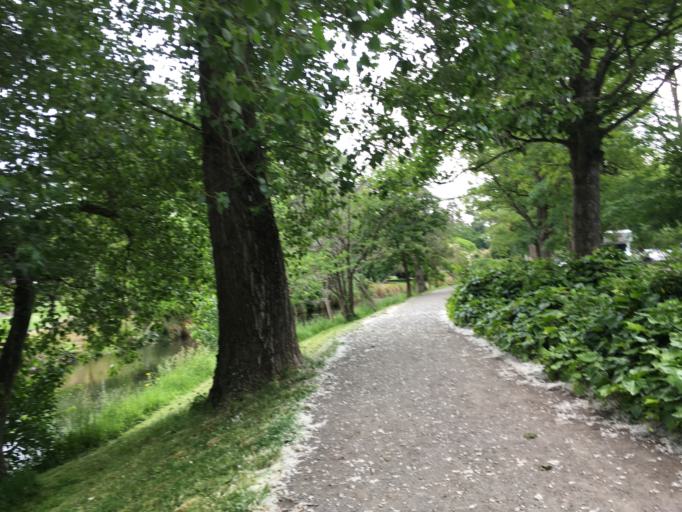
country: NZ
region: Canterbury
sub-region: Christchurch City
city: Christchurch
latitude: -43.5292
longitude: 172.6224
